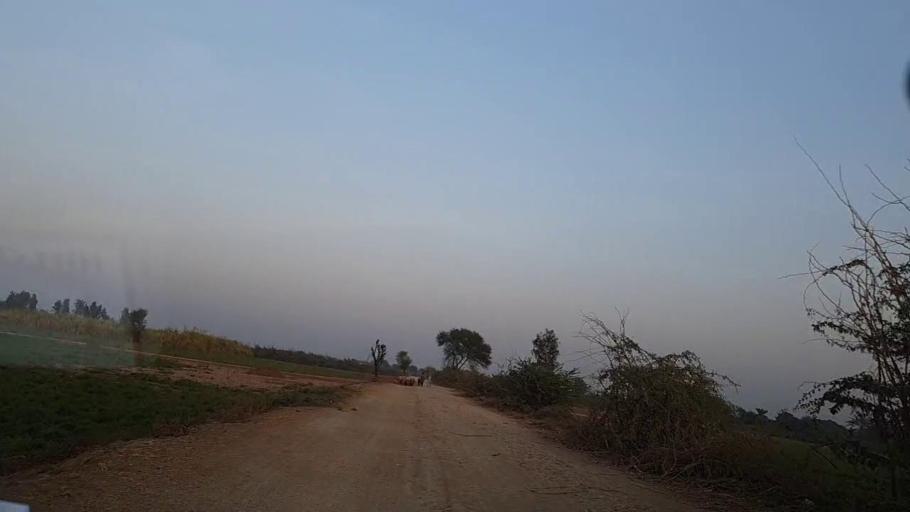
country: PK
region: Sindh
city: Tando Ghulam Ali
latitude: 25.1573
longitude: 68.9271
